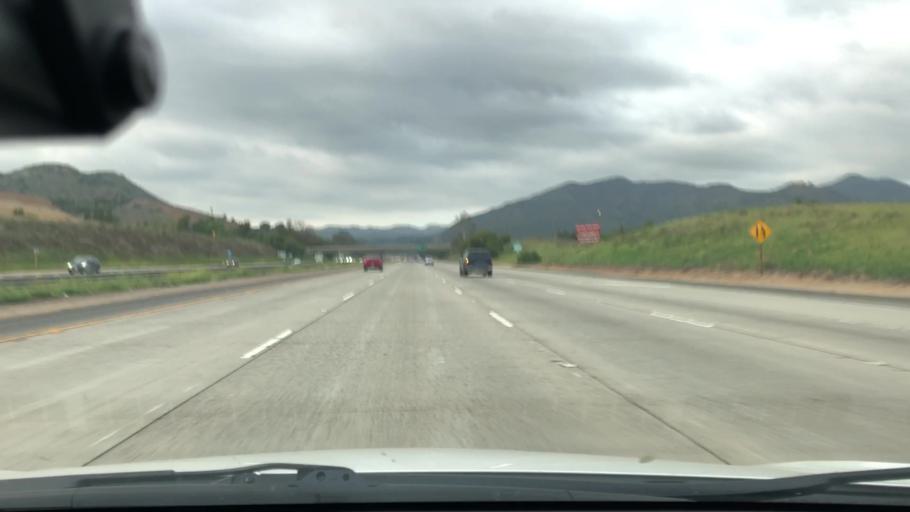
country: US
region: California
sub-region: San Diego County
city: Rainbow
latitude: 33.3370
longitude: -117.1590
